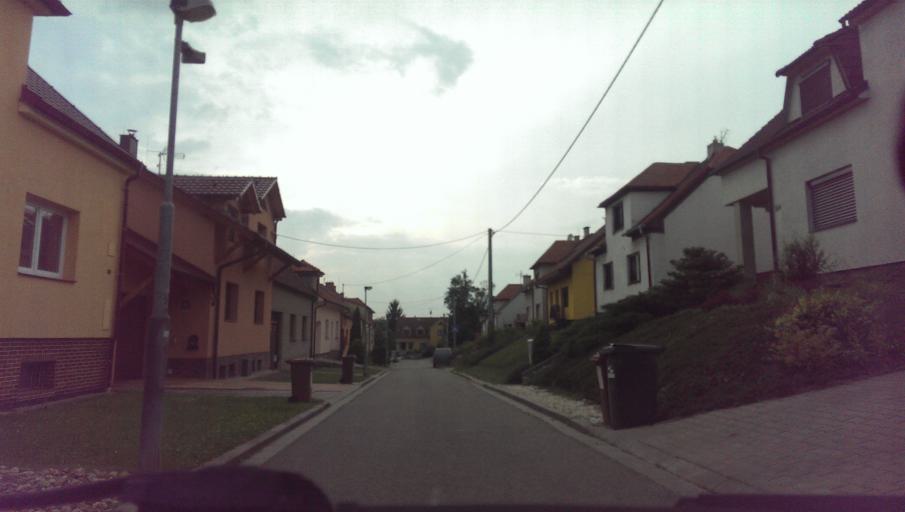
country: CZ
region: Zlin
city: Popovice
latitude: 49.0340
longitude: 17.5093
